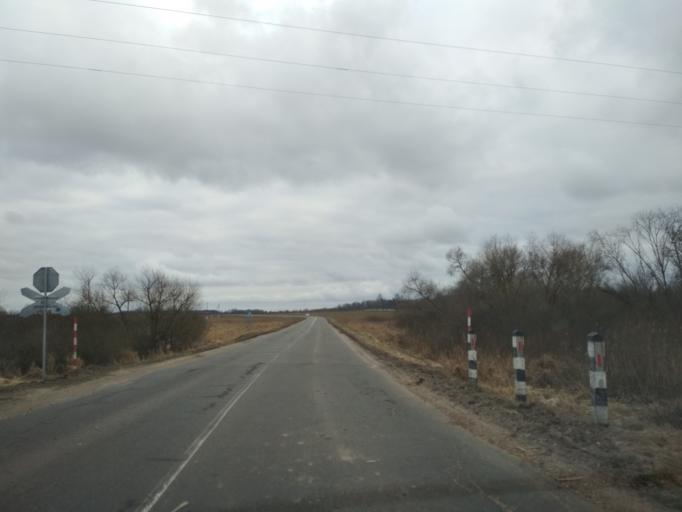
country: BY
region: Minsk
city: Druzhny
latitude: 53.5874
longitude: 27.9001
